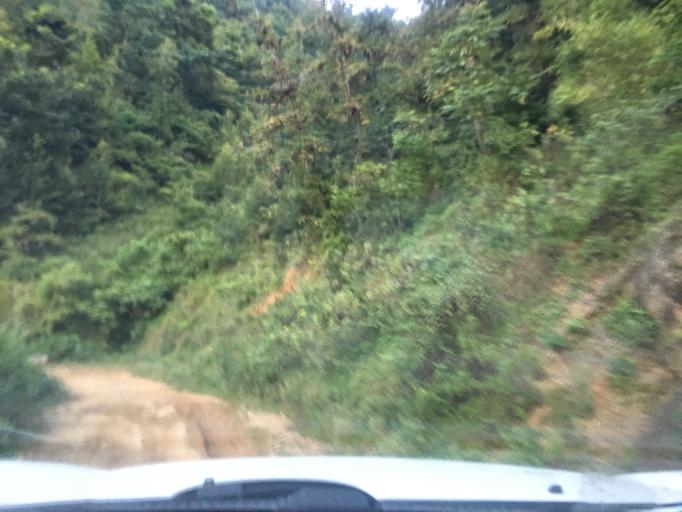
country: CN
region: Guangxi Zhuangzu Zizhiqu
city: Xinzhou
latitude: 25.3540
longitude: 105.7445
